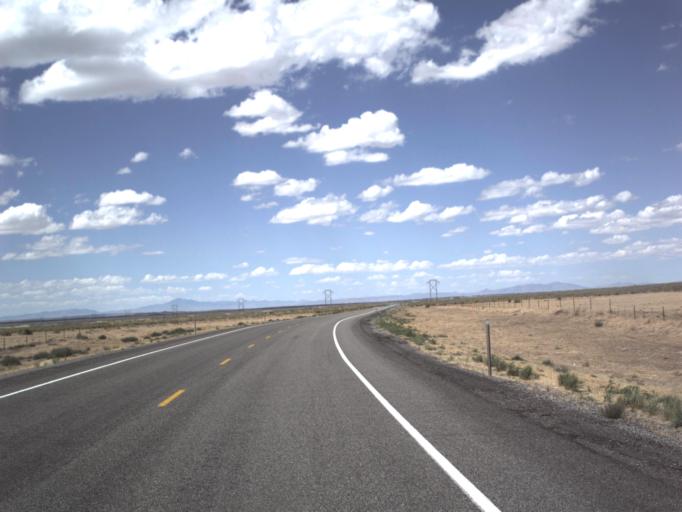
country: US
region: Utah
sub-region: Millard County
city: Fillmore
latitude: 39.1500
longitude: -112.3959
